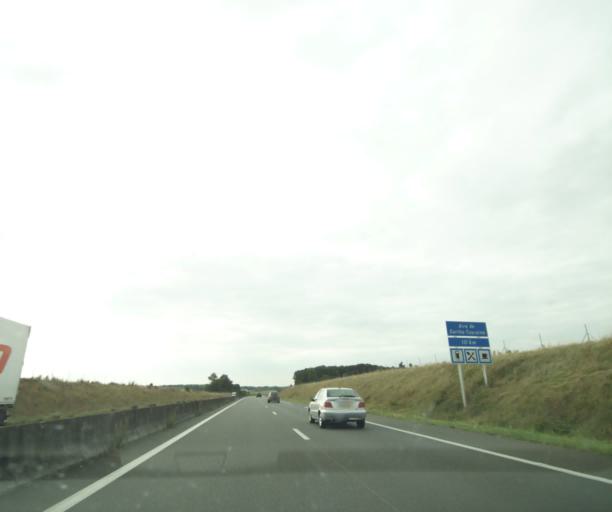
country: FR
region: Centre
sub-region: Departement d'Indre-et-Loire
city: Neuvy-le-Roi
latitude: 47.5867
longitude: 0.5599
